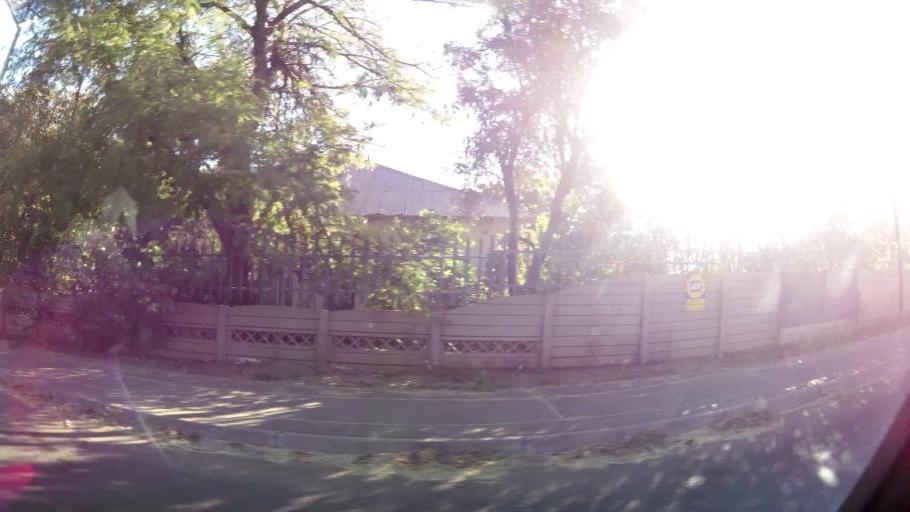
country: ZA
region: Gauteng
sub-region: City of Tshwane Metropolitan Municipality
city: Pretoria
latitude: -25.7060
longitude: 28.1704
